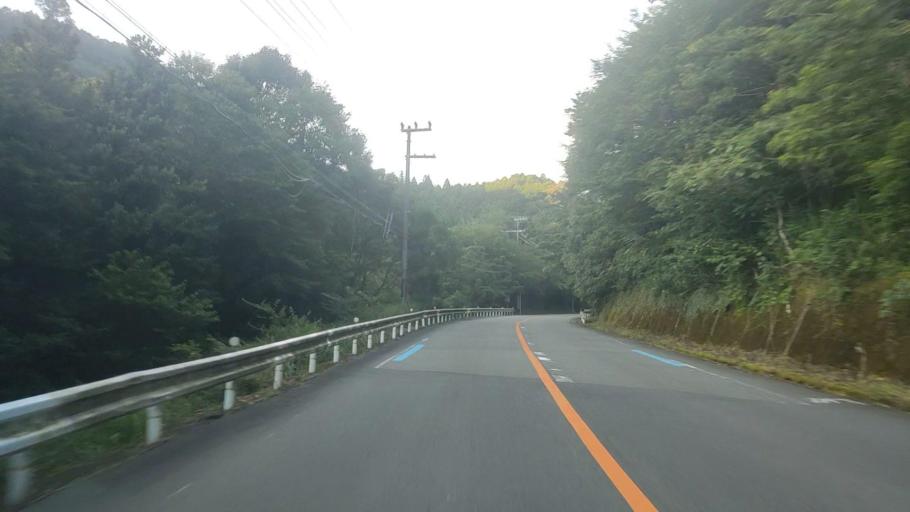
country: JP
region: Wakayama
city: Tanabe
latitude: 33.8184
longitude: 135.6210
